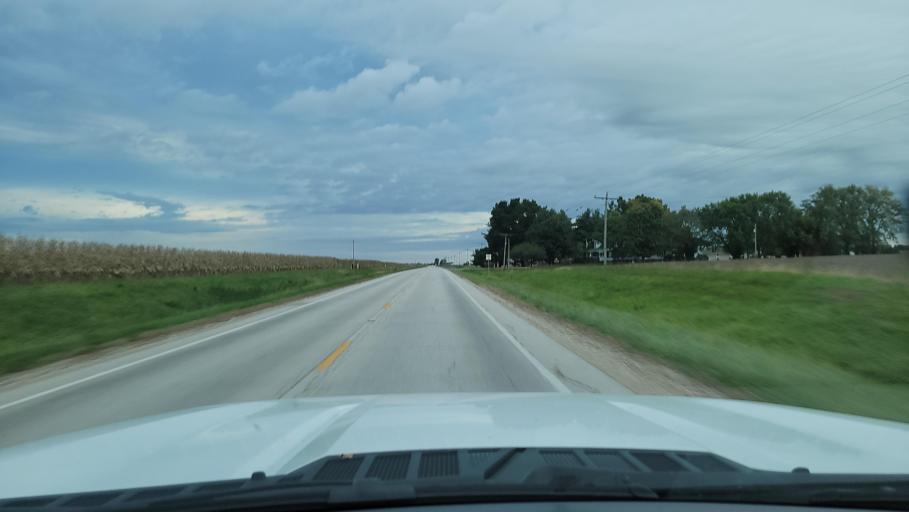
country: US
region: Illinois
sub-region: Schuyler County
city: Rushville
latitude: 40.0648
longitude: -90.6152
